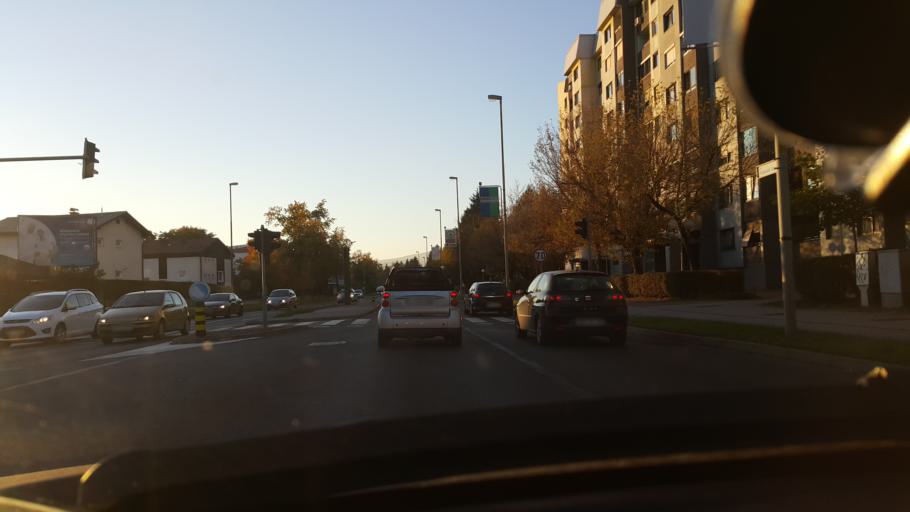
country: SI
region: Maribor
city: Maribor
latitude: 46.5435
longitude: 15.6317
